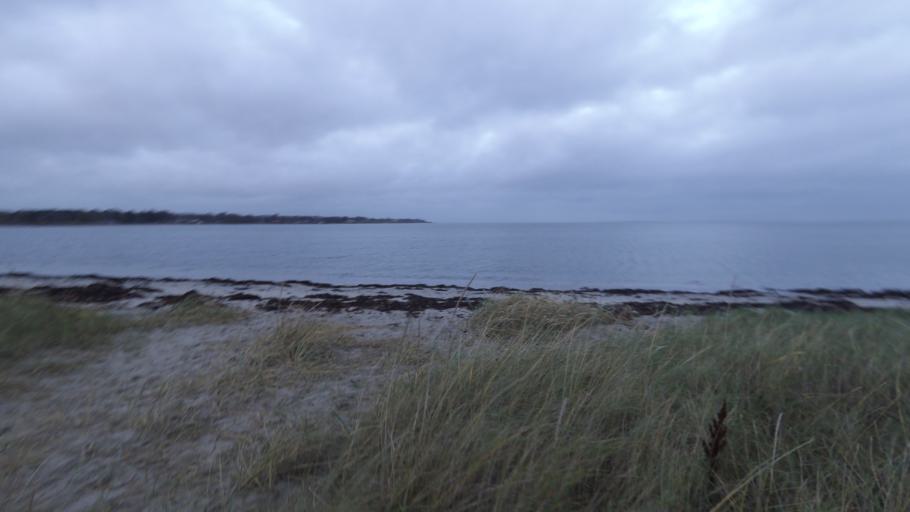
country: DK
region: Central Jutland
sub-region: Arhus Kommune
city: Beder
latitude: 56.0232
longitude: 10.2712
